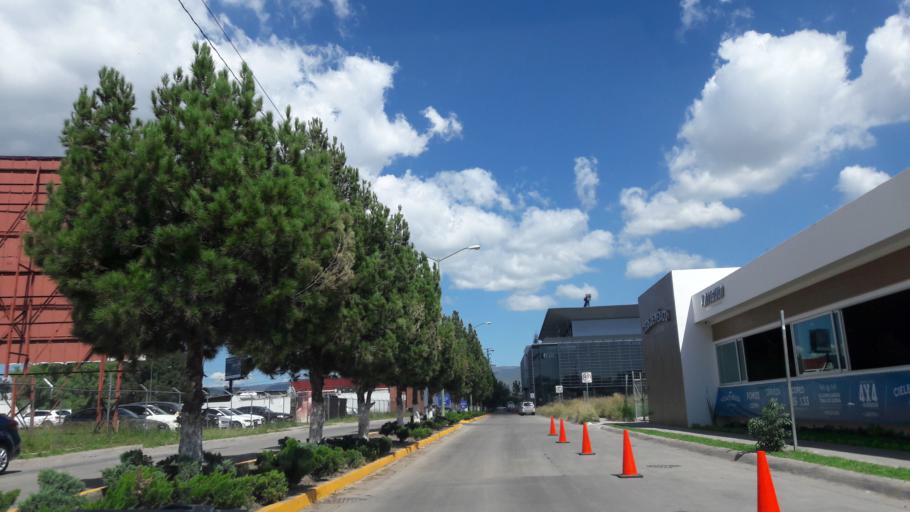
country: MX
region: Guanajuato
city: Leon
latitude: 21.1532
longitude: -101.6881
